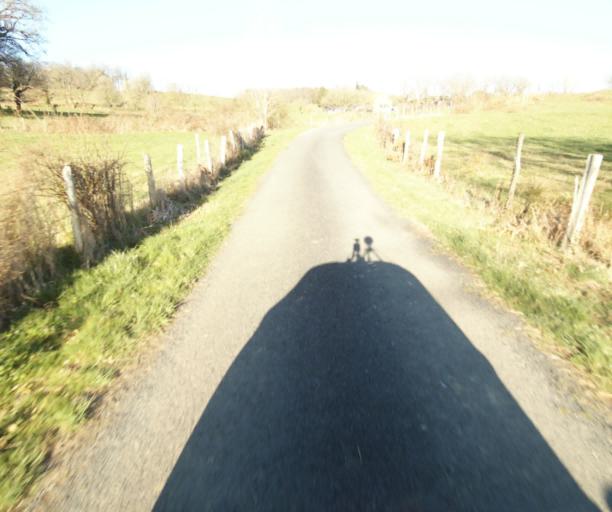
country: FR
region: Limousin
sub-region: Departement de la Correze
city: Saint-Clement
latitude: 45.3572
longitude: 1.6936
